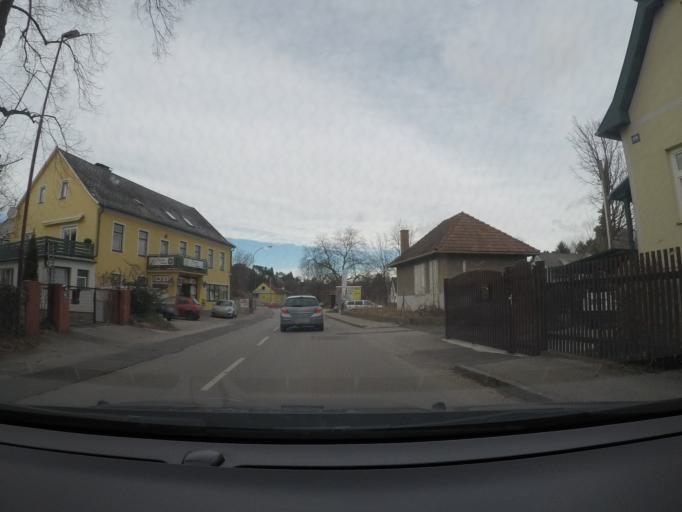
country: AT
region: Lower Austria
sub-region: Politischer Bezirk Neunkirchen
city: Pitten
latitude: 47.7190
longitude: 16.1841
